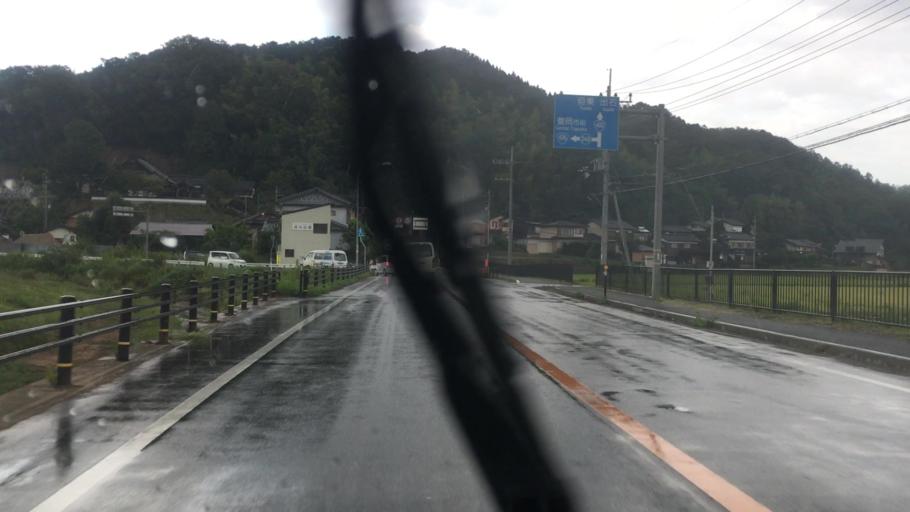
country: JP
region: Hyogo
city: Toyooka
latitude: 35.4853
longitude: 134.8169
